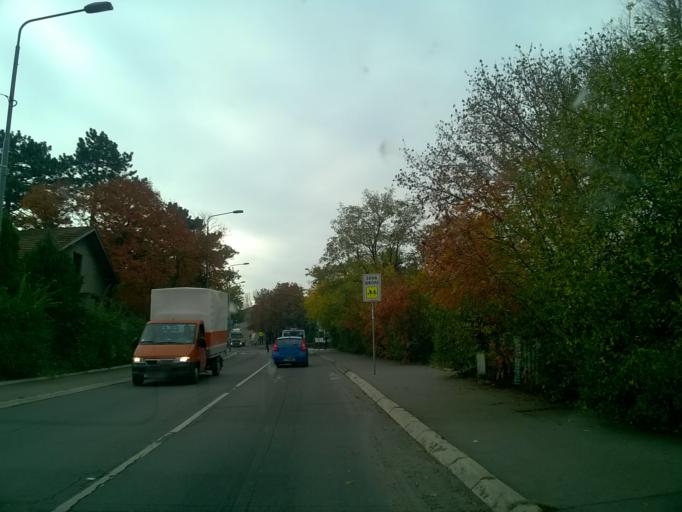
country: RS
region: Central Serbia
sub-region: Belgrade
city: Palilula
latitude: 44.7990
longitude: 20.4995
